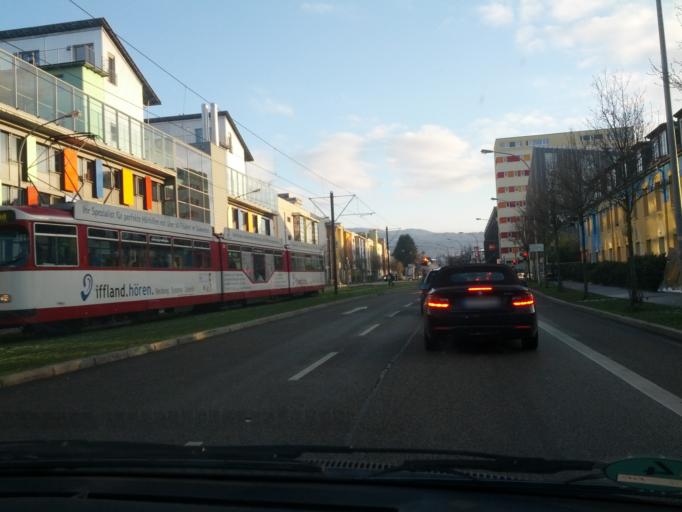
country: DE
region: Baden-Wuerttemberg
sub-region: Freiburg Region
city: Merzhausen
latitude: 47.9751
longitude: 7.8285
